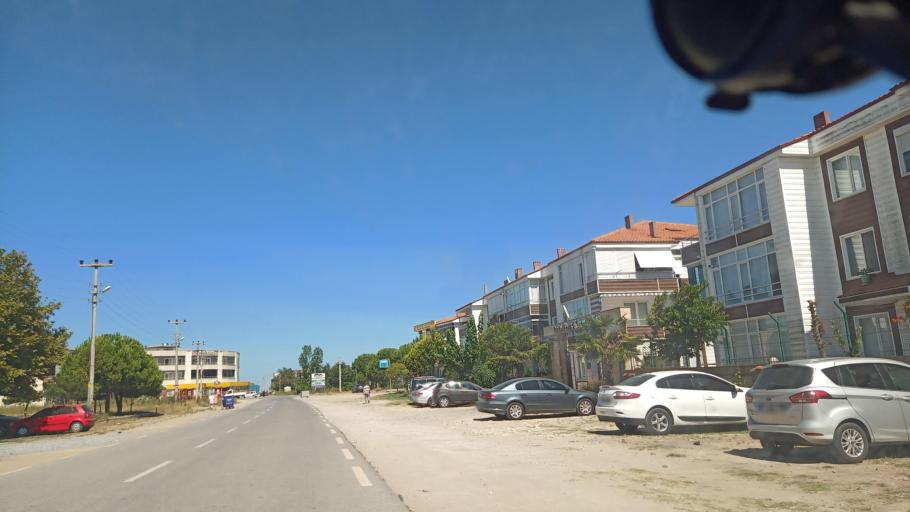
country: TR
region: Sakarya
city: Karasu
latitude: 41.1191
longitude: 30.6534
